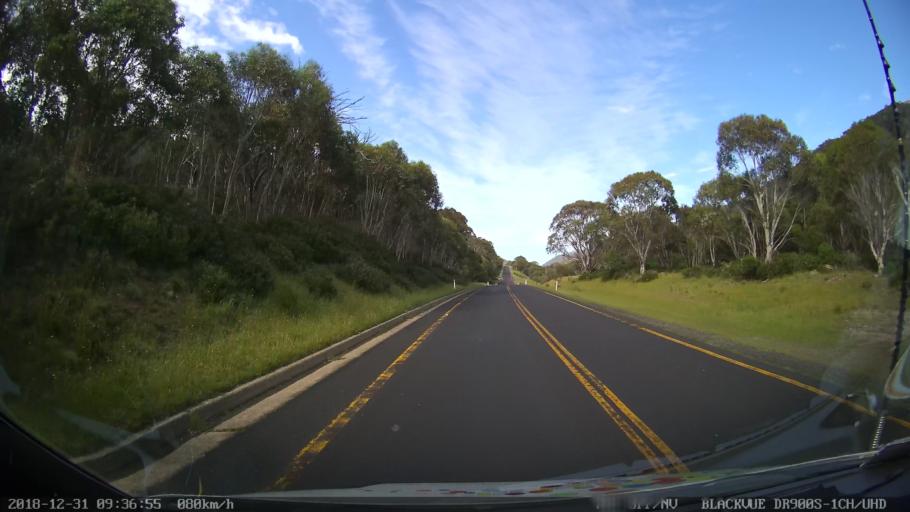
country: AU
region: New South Wales
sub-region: Snowy River
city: Jindabyne
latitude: -36.4625
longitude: 148.3817
